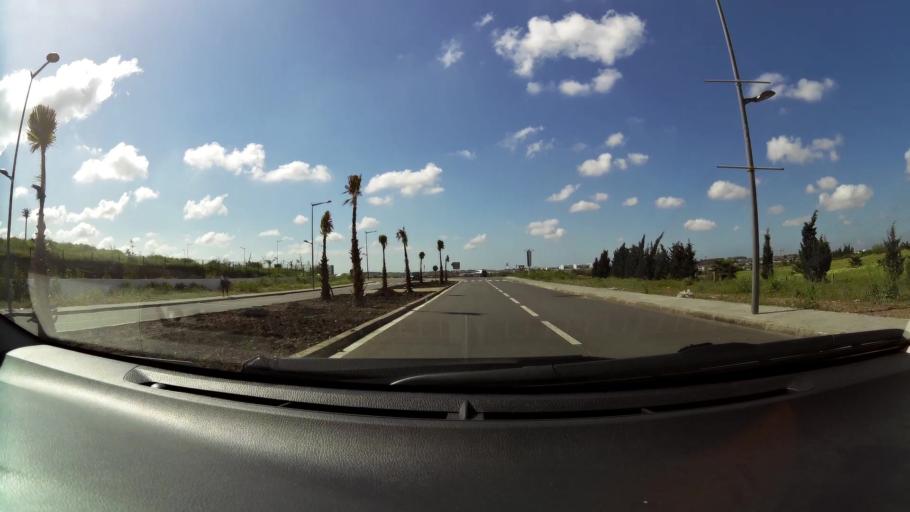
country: MA
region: Grand Casablanca
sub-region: Nouaceur
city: Bouskoura
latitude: 33.4768
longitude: -7.6041
